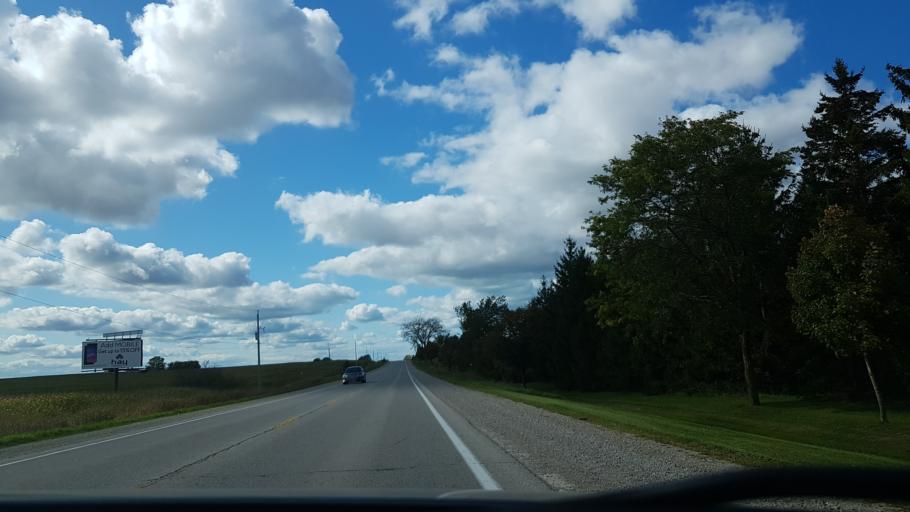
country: CA
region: Ontario
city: South Huron
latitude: 43.3498
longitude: -81.5987
